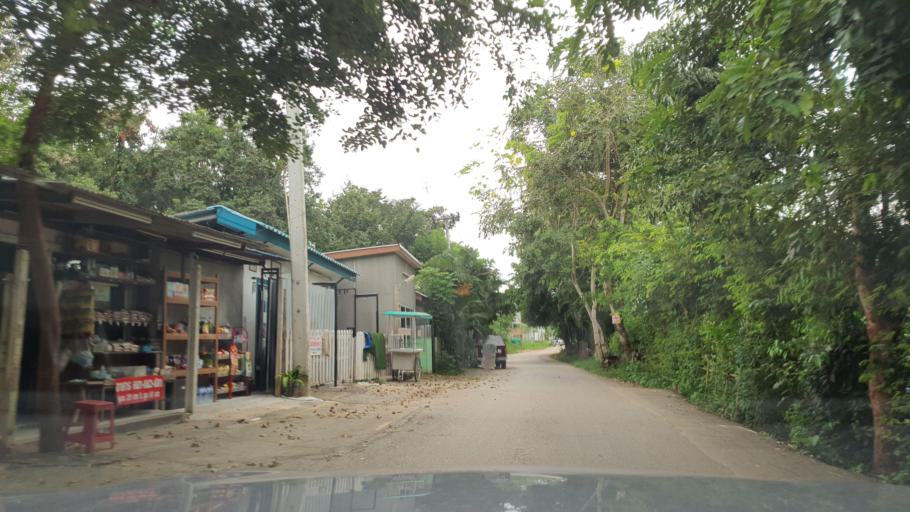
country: TH
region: Chiang Mai
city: San Sai
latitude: 18.9206
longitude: 98.9394
